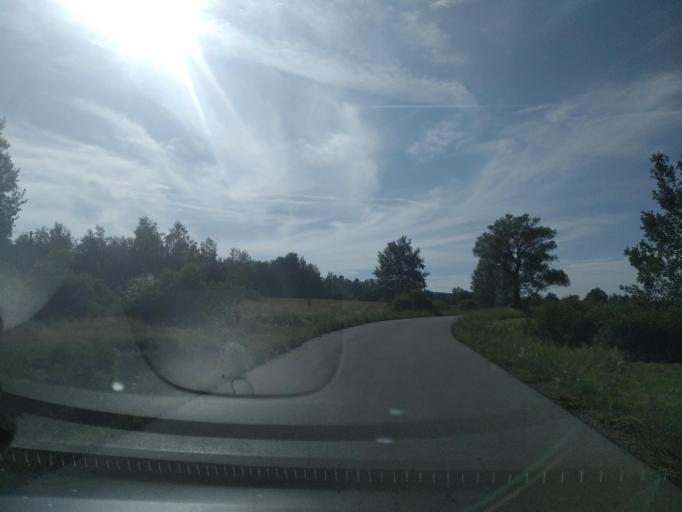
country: PL
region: Subcarpathian Voivodeship
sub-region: Powiat krosnienski
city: Jasliska
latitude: 49.4064
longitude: 21.8674
